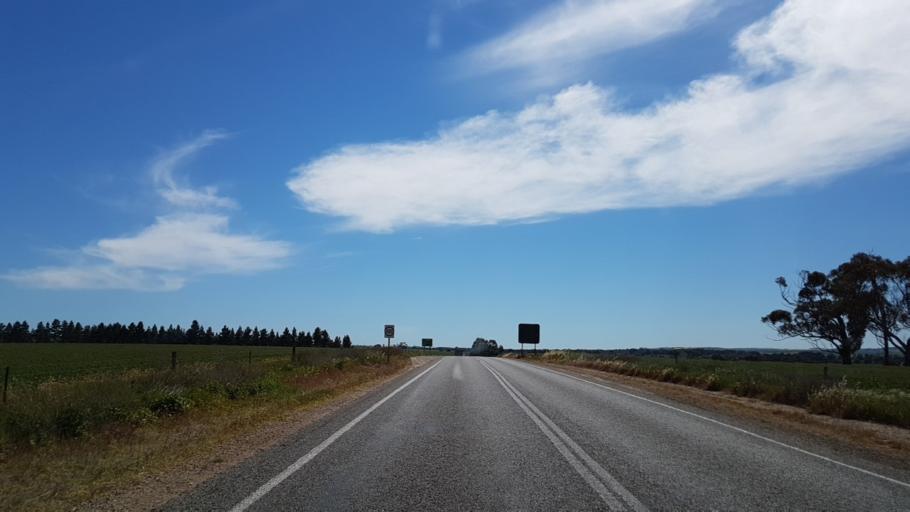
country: AU
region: South Australia
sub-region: Light
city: Kapunda
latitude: -34.2296
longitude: 138.7385
